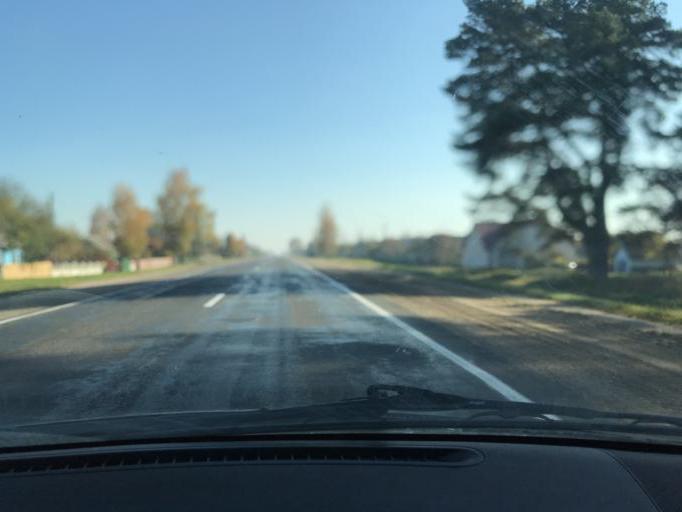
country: BY
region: Brest
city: Lyakhavichy
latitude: 52.9623
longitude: 26.4493
